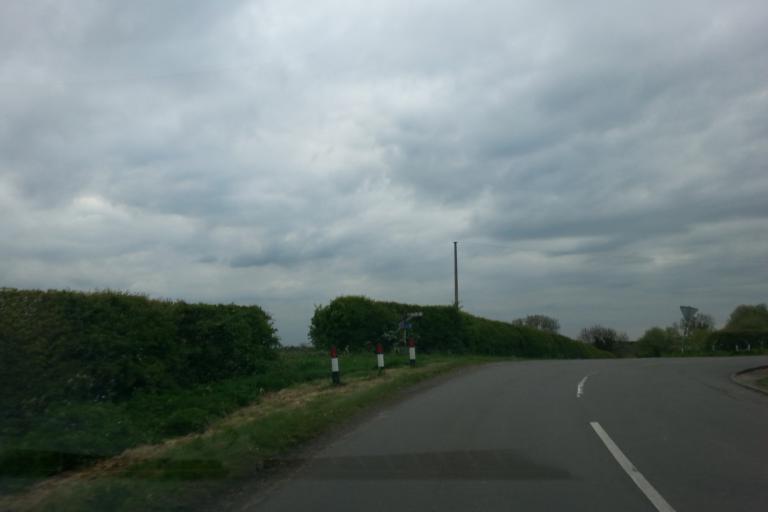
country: GB
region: England
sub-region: Nottinghamshire
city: Farndon
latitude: 53.0072
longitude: -0.8164
